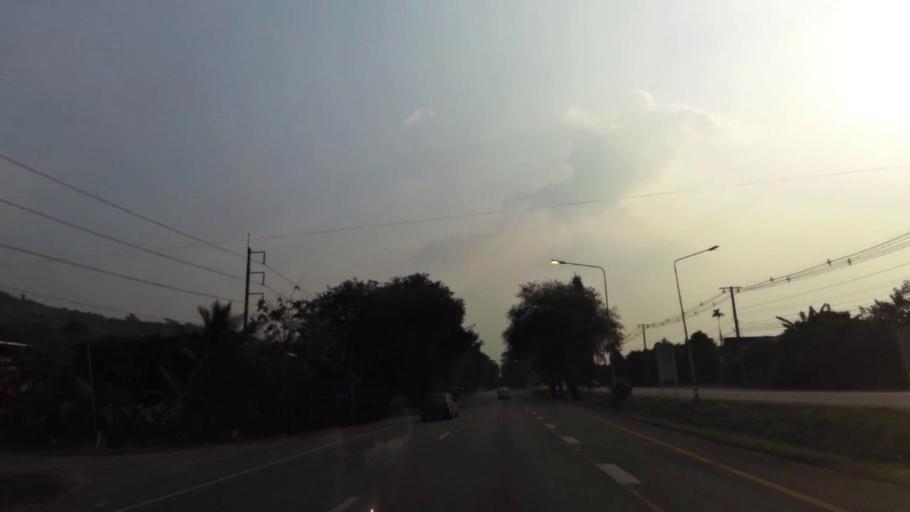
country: TH
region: Chanthaburi
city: Chanthaburi
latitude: 12.5684
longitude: 102.1620
